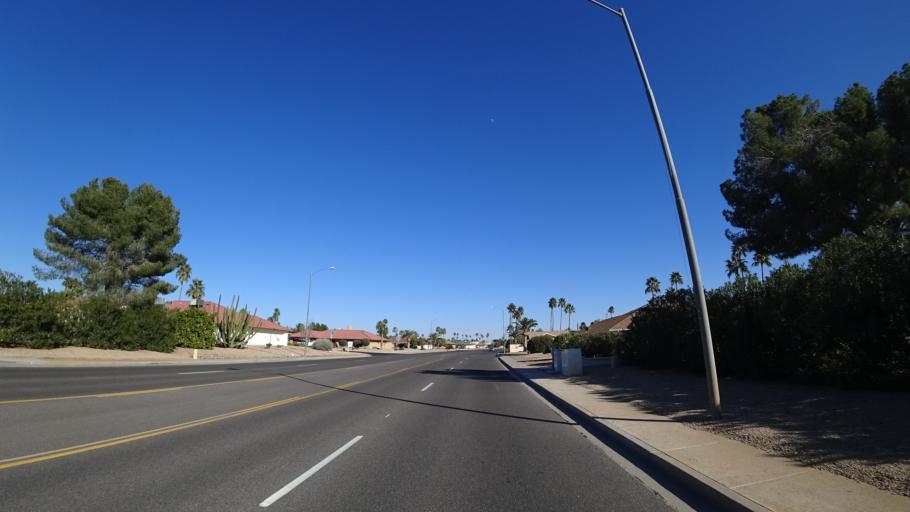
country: US
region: Arizona
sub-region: Maricopa County
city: Sun City West
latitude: 33.6787
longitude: -112.3496
